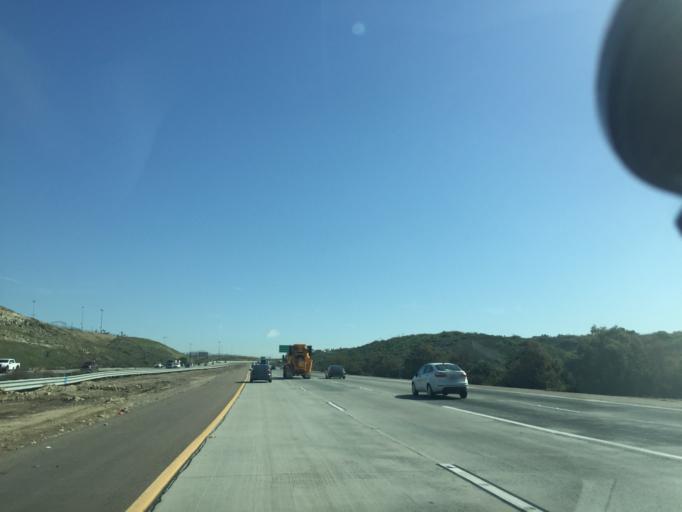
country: MX
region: Baja California
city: Tijuana
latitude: 32.5680
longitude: -117.0314
